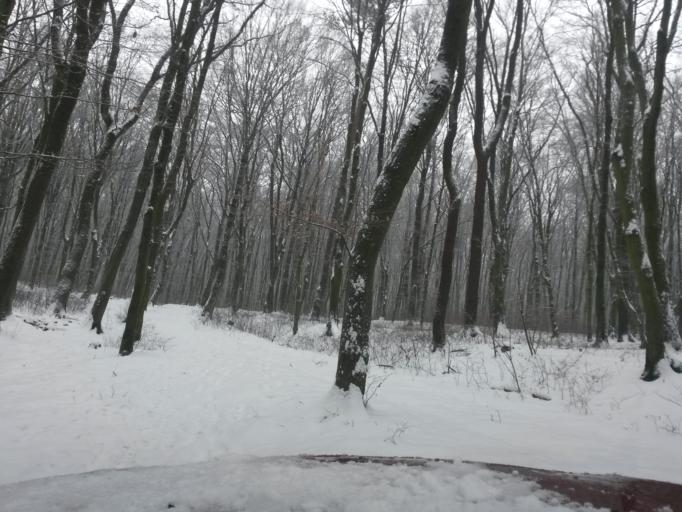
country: SK
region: Kosicky
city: Kosice
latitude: 48.7195
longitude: 21.3089
